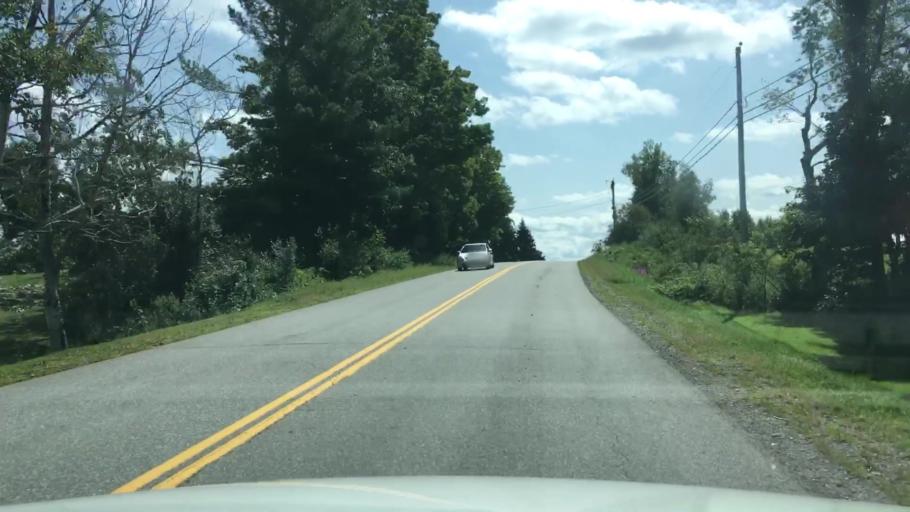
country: US
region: Maine
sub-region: Kennebec County
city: Manchester
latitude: 44.3517
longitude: -69.8141
